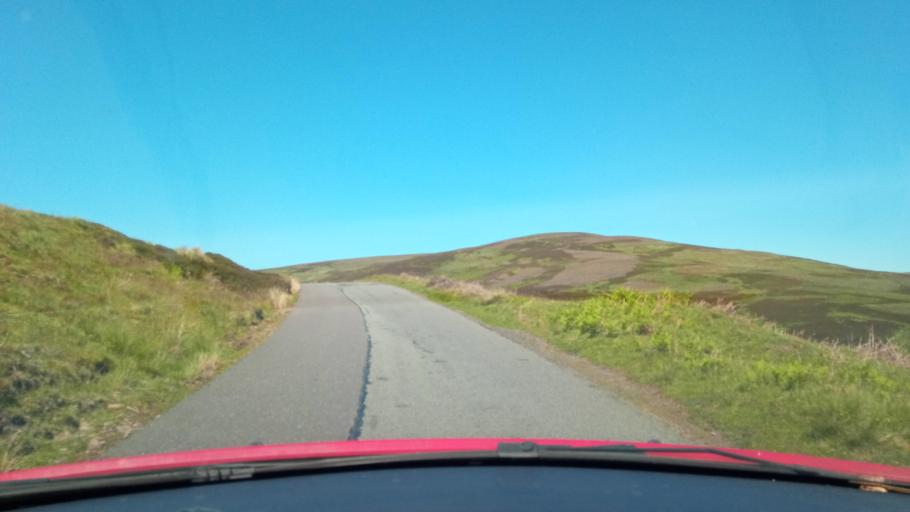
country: GB
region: Scotland
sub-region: East Lothian
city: East Linton
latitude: 55.8436
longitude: -2.5836
